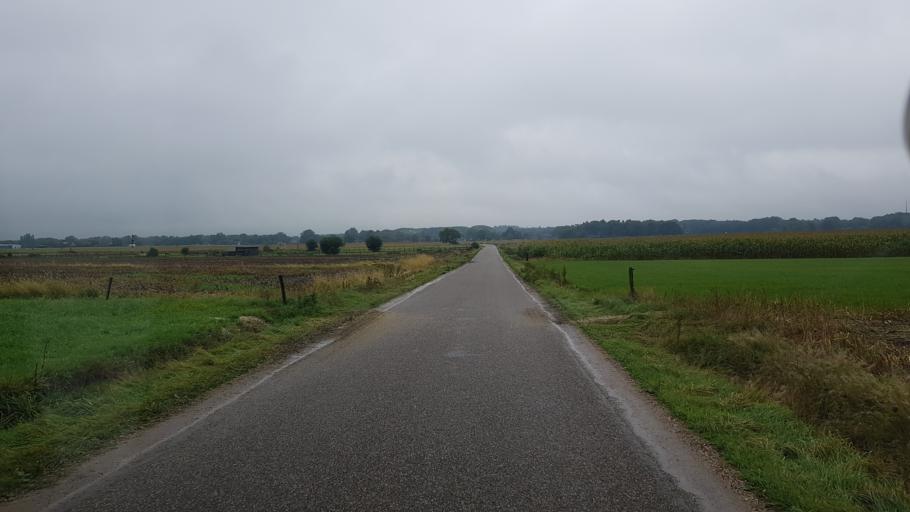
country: NL
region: Gelderland
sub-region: Gemeente Apeldoorn
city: Beekbergen
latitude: 52.1560
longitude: 5.9880
